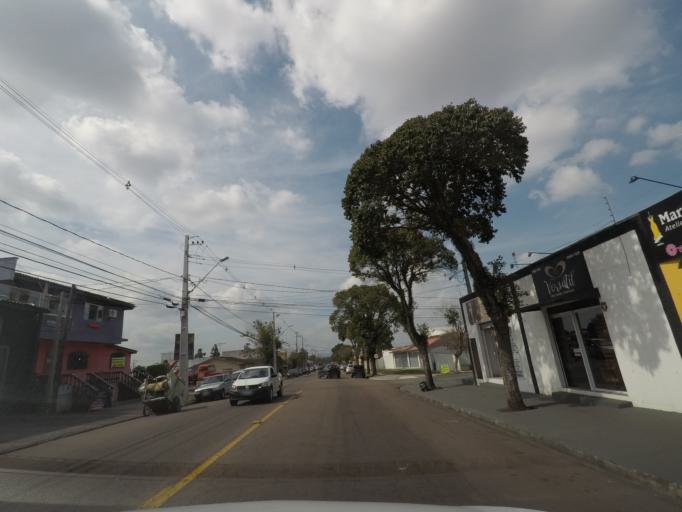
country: BR
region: Parana
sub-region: Pinhais
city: Pinhais
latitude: -25.4700
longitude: -49.2077
